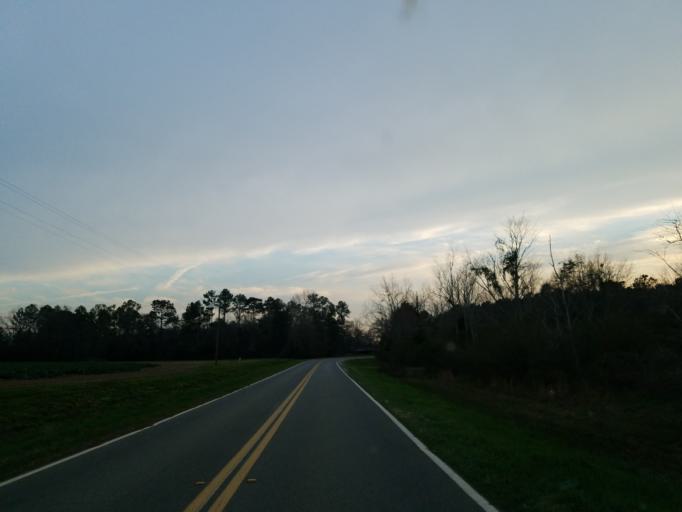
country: US
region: Georgia
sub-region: Cook County
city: Sparks
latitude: 31.0772
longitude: -83.6165
